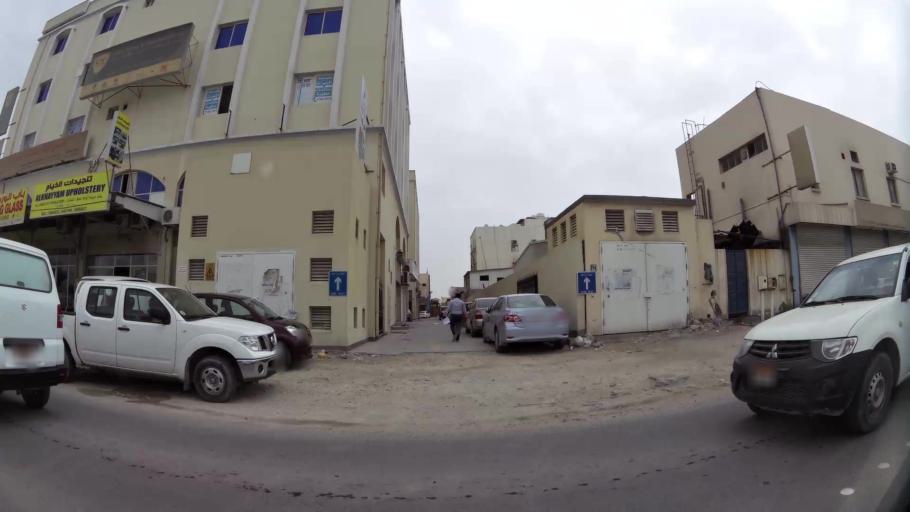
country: BH
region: Northern
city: Madinat `Isa
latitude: 26.1765
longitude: 50.5347
